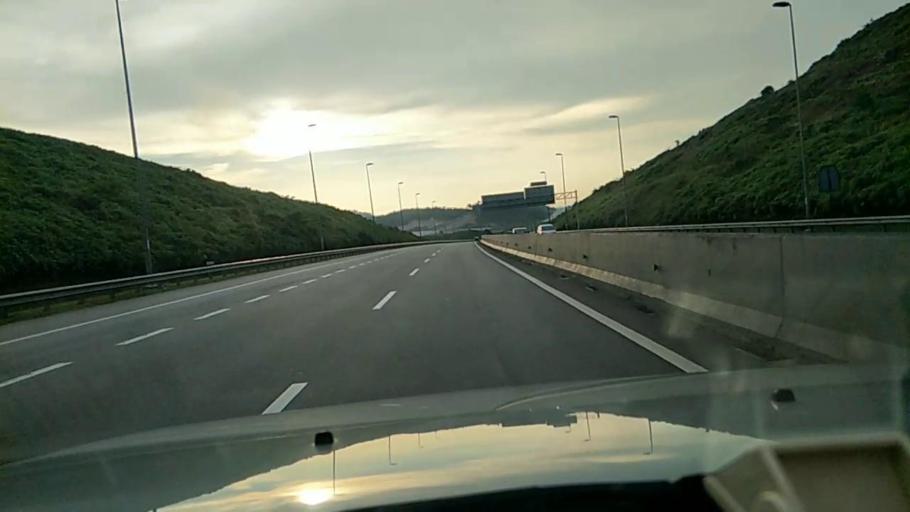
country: MY
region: Selangor
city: Batu Arang
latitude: 3.2735
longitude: 101.4589
